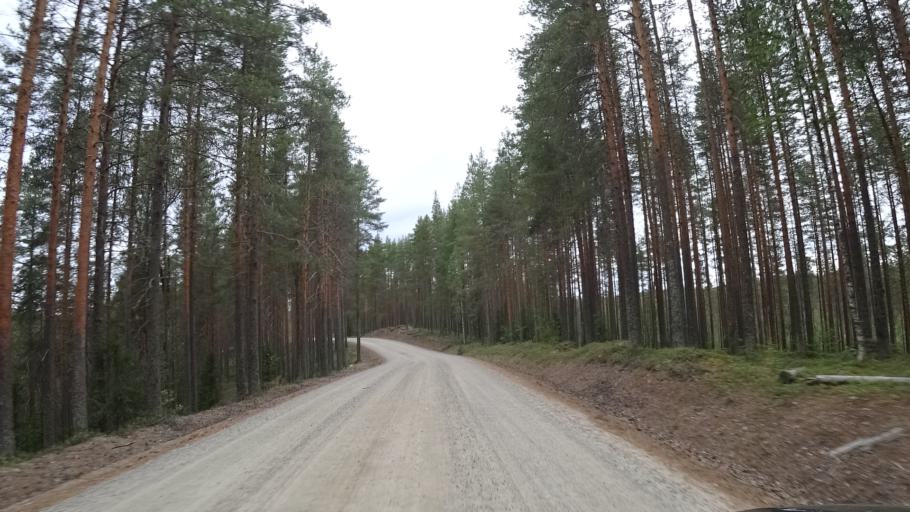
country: FI
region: North Karelia
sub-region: Pielisen Karjala
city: Lieksa
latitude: 63.2447
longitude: 30.3420
